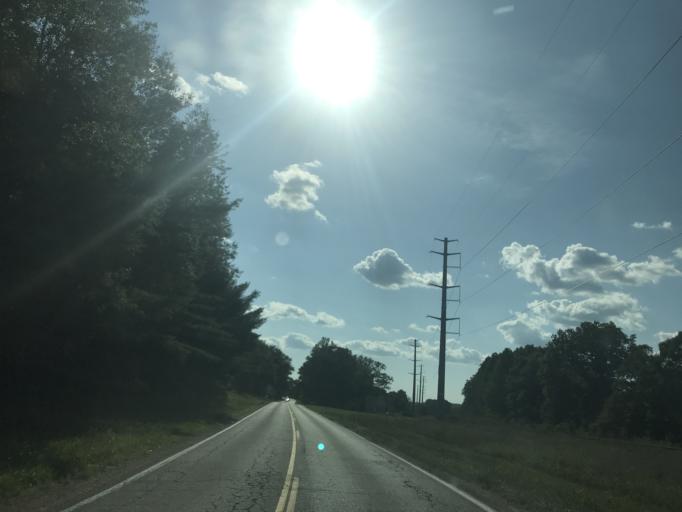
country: US
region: Michigan
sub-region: Newaygo County
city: Newaygo
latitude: 43.4273
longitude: -85.7773
